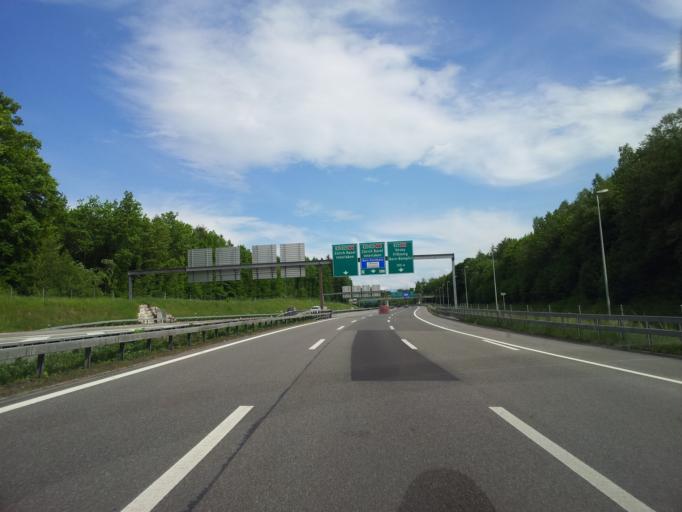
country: CH
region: Bern
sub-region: Bern-Mittelland District
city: Koniz
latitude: 46.9539
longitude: 7.3949
